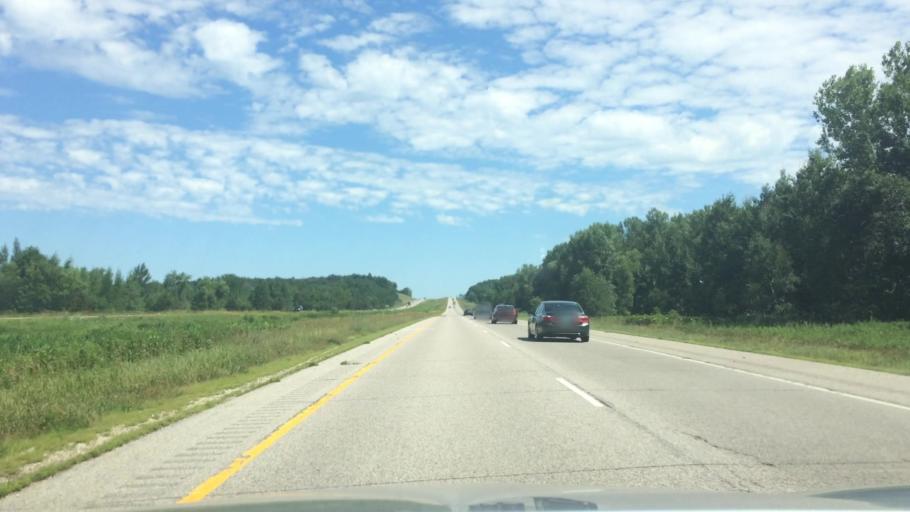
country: US
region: Wisconsin
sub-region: Marquette County
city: Westfield
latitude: 43.7720
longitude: -89.4844
